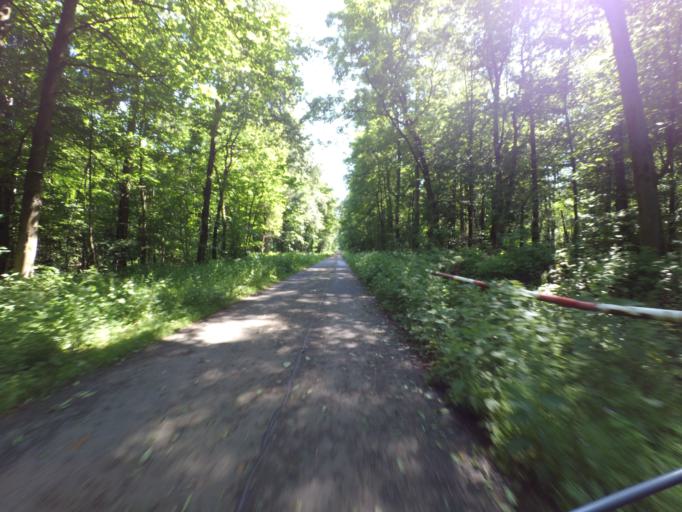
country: DE
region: Rheinland-Pfalz
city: Spesenroth
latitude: 50.0594
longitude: 7.4518
